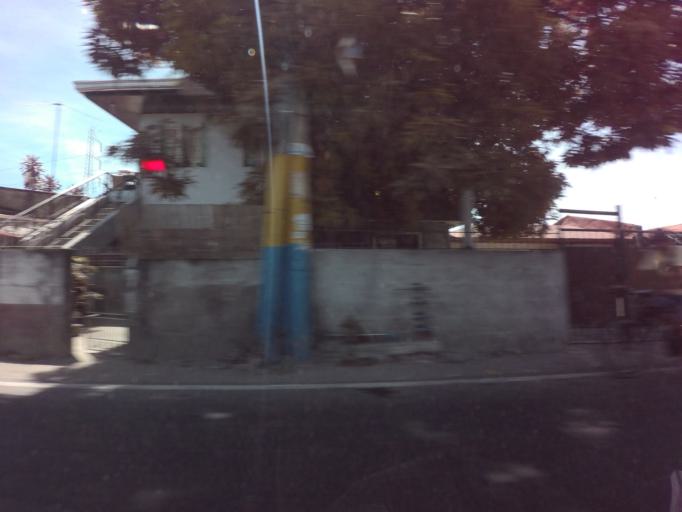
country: PH
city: Sambayanihan People's Village
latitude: 14.4623
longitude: 121.0548
